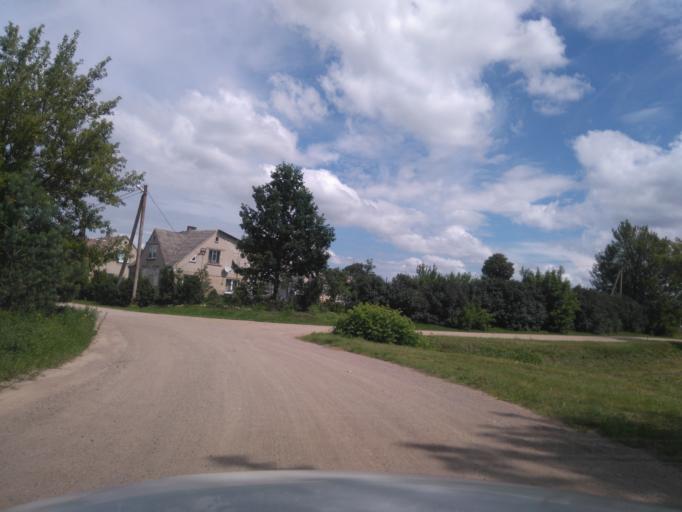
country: LT
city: Virbalis
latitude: 54.6246
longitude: 22.8125
